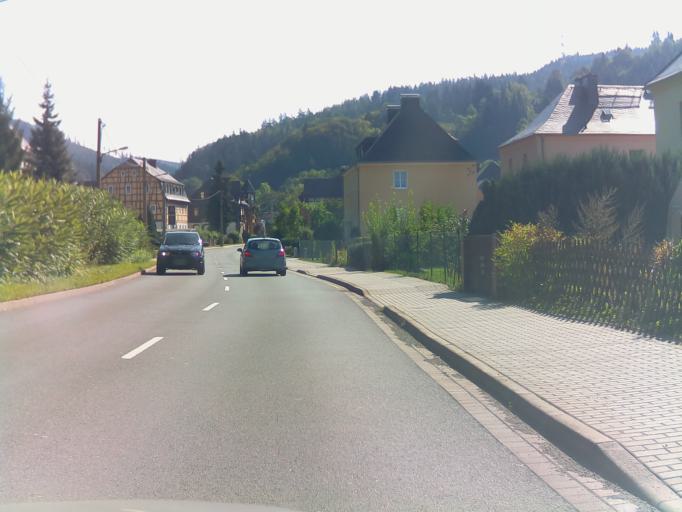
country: DE
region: Thuringia
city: Leutenberg
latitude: 50.5663
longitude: 11.4490
